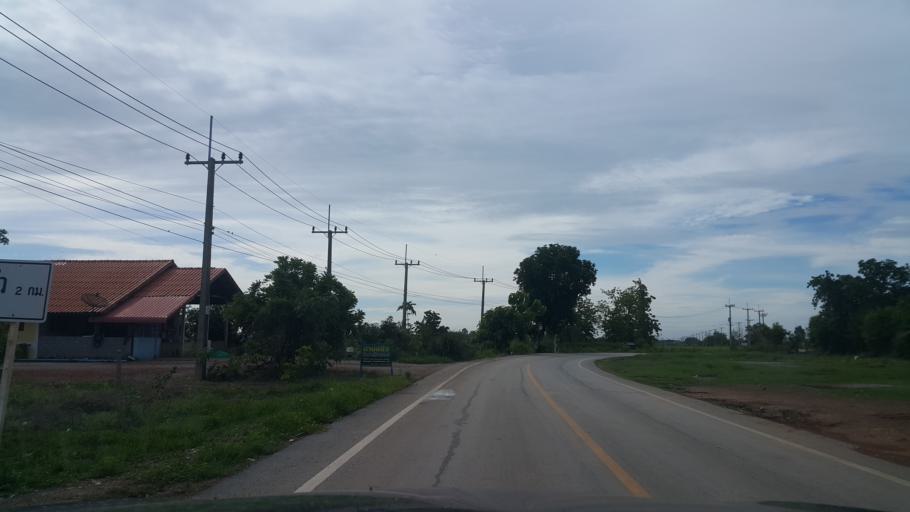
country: TH
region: Sukhothai
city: Si Nakhon
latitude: 17.2787
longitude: 99.9748
